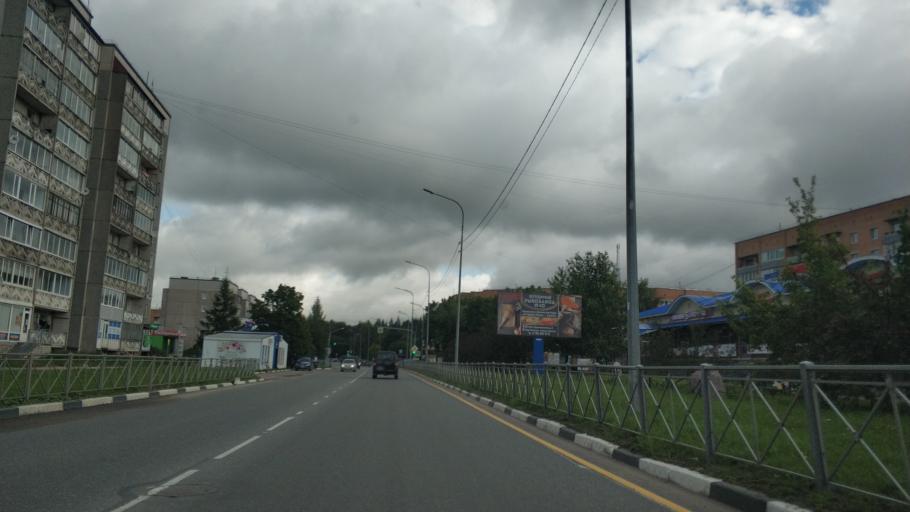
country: RU
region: Republic of Karelia
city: Sortavala
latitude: 61.7092
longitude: 30.6990
